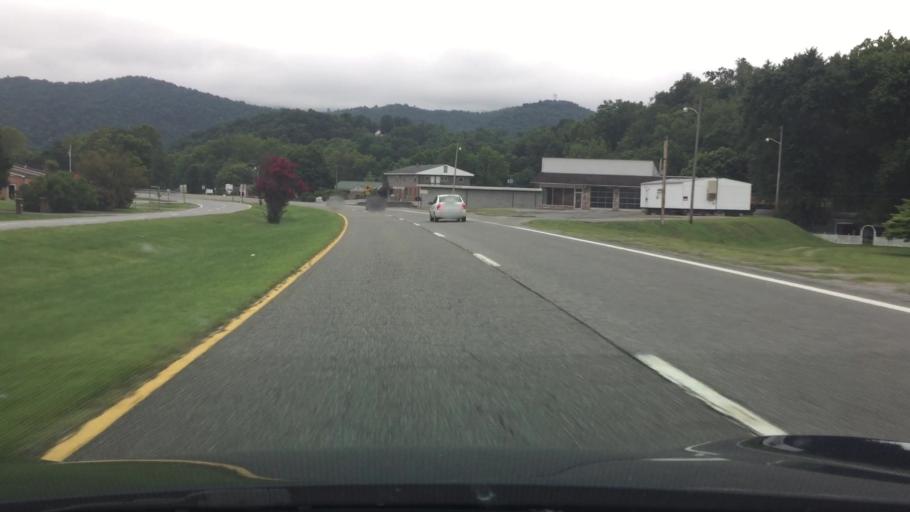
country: US
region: Virginia
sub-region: Montgomery County
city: Shawsville
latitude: 37.1682
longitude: -80.2593
